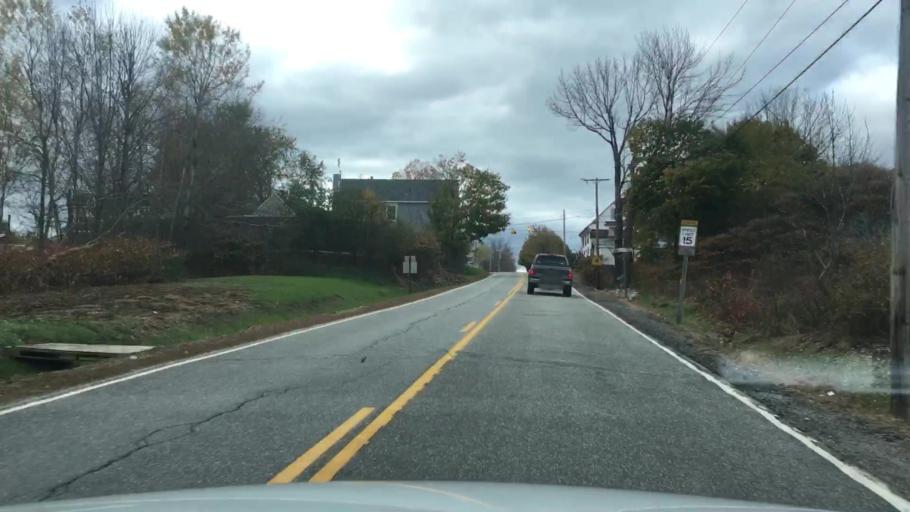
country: US
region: Maine
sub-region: Kennebec County
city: Monmouth
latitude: 44.1328
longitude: -69.9635
